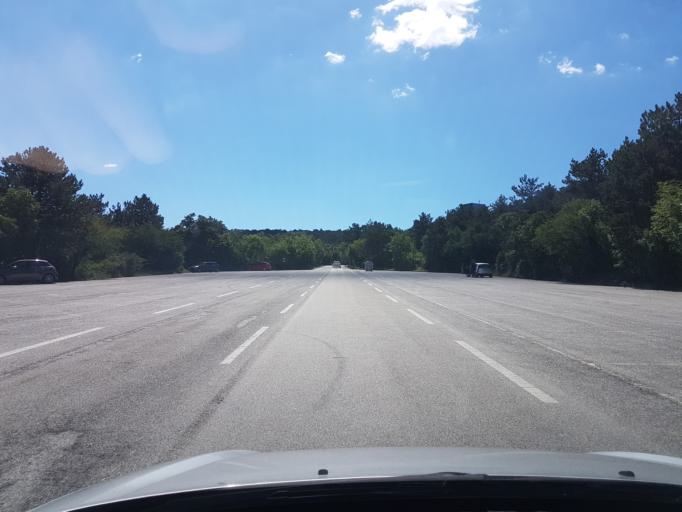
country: IT
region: Friuli Venezia Giulia
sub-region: Provincia di Trieste
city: Prosecco-Contovello
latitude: 45.6973
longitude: 13.7468
